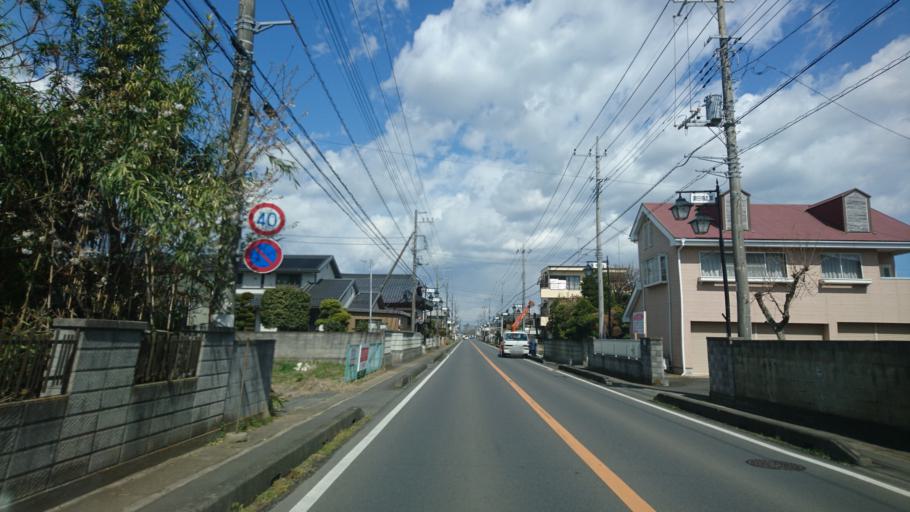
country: JP
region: Ibaraki
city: Ishige
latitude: 36.1865
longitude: 139.9568
